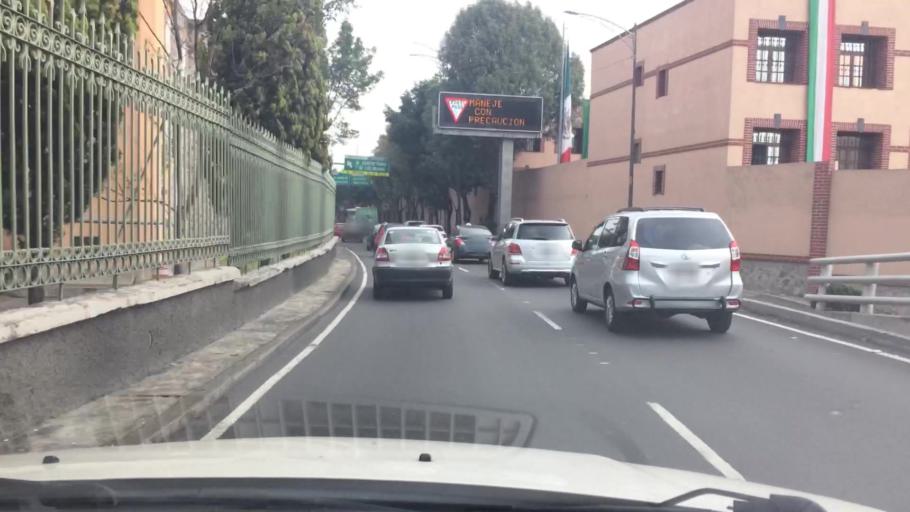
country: MX
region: Mexico City
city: Polanco
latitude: 19.4040
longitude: -99.1917
